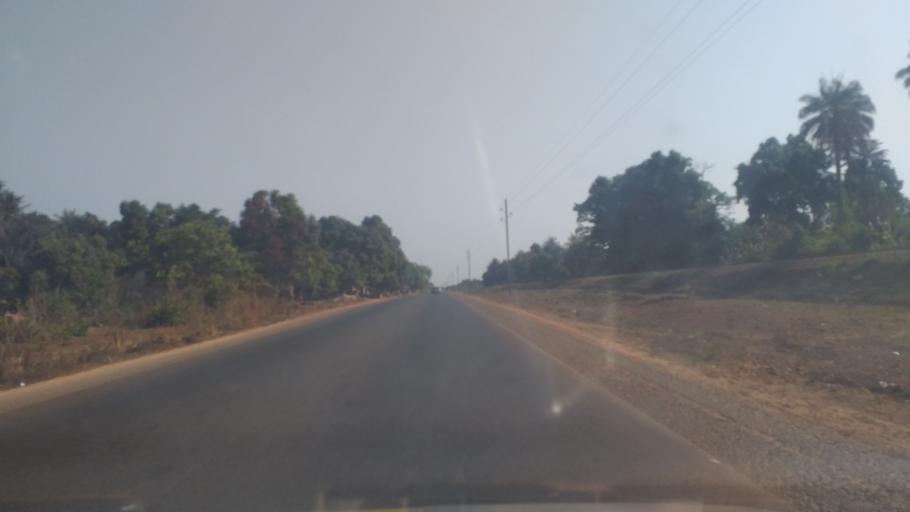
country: GN
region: Boke
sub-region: Boke Prefecture
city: Kamsar
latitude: 10.7150
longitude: -14.5223
